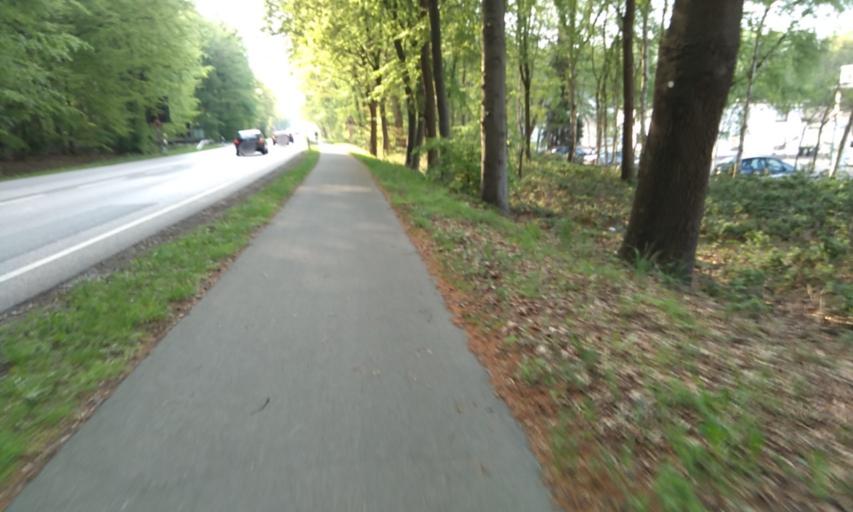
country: DE
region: Lower Saxony
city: Buxtehude
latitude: 53.4708
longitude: 9.6683
